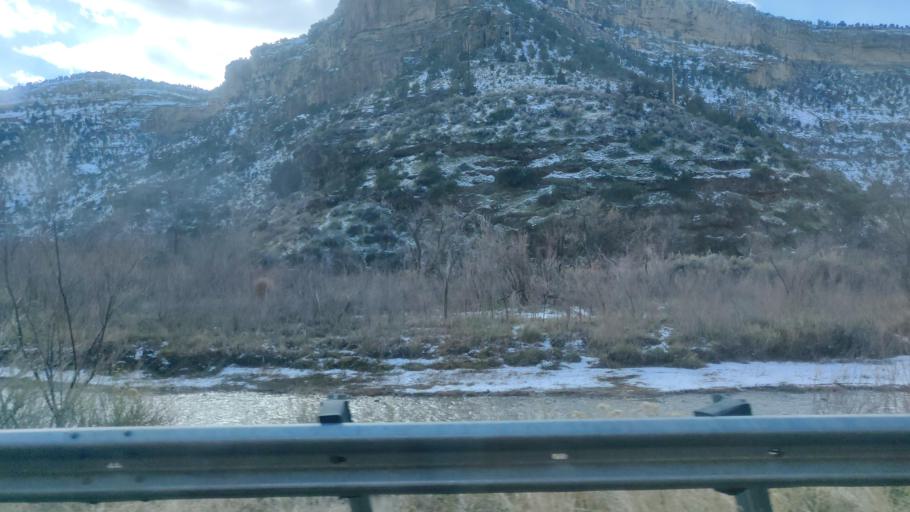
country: US
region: Colorado
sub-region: Mesa County
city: Palisade
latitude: 39.1923
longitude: -108.2493
